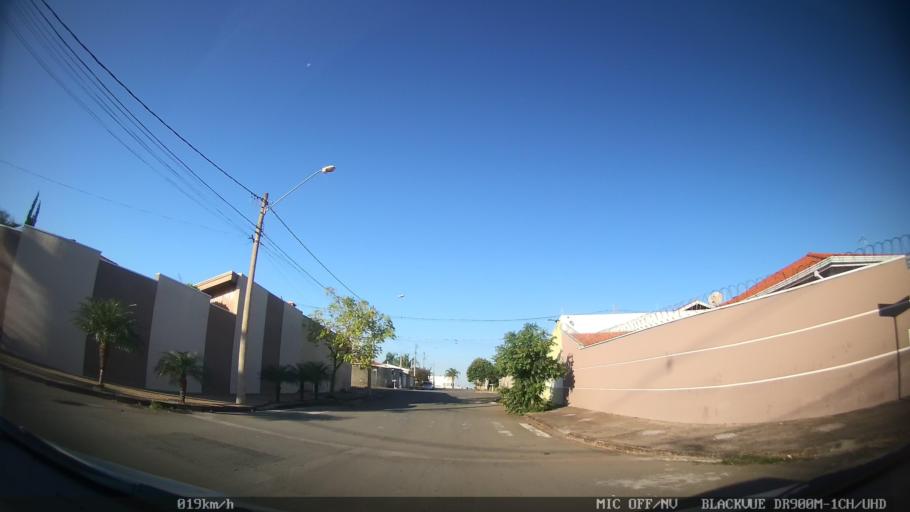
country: BR
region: Sao Paulo
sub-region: Nova Odessa
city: Nova Odessa
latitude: -22.7741
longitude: -47.2779
